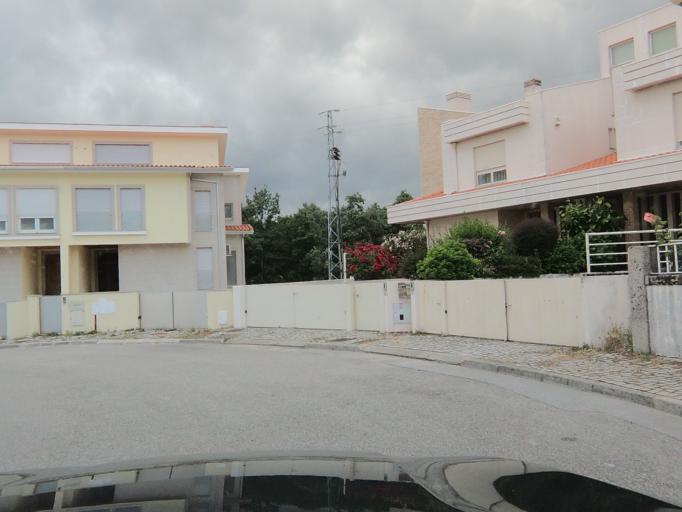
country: PT
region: Vila Real
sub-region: Vila Real
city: Vila Real
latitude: 41.3119
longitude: -7.7218
